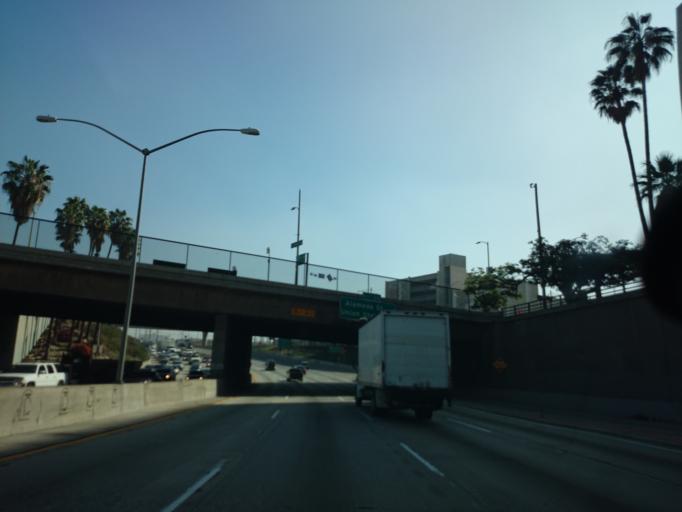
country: US
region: California
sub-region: Los Angeles County
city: Los Angeles
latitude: 34.0545
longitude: -118.2386
